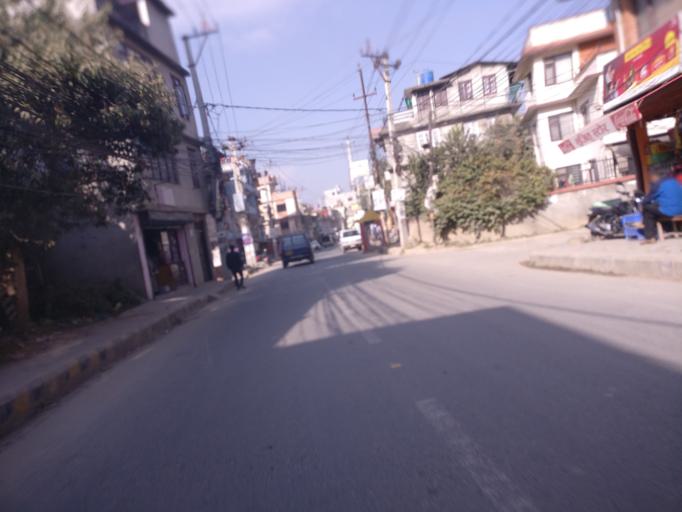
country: NP
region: Central Region
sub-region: Bagmati Zone
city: Patan
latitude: 27.6745
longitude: 85.3079
